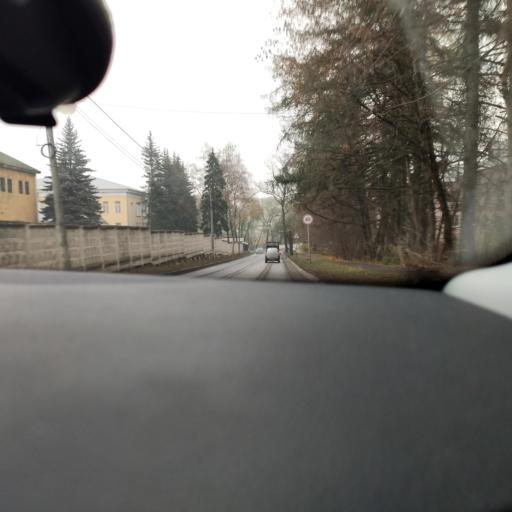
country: RU
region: Moskovskaya
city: Nakhabino
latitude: 55.8416
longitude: 37.1601
